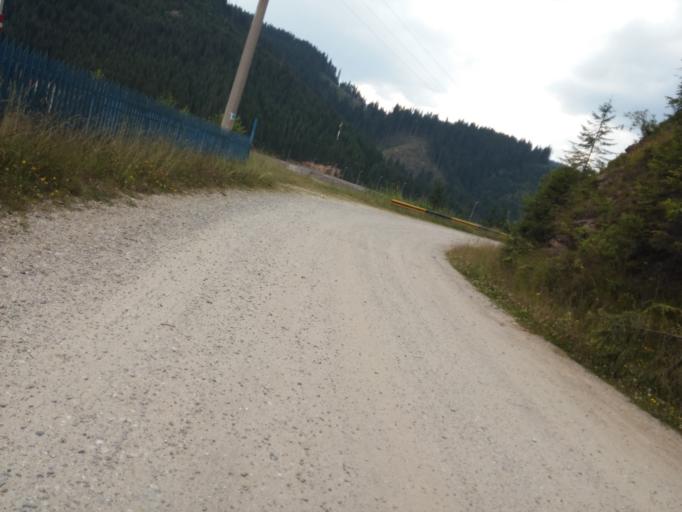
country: RO
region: Valcea
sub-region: Comuna Voineasa
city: Voineasa
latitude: 45.4442
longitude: 23.7685
